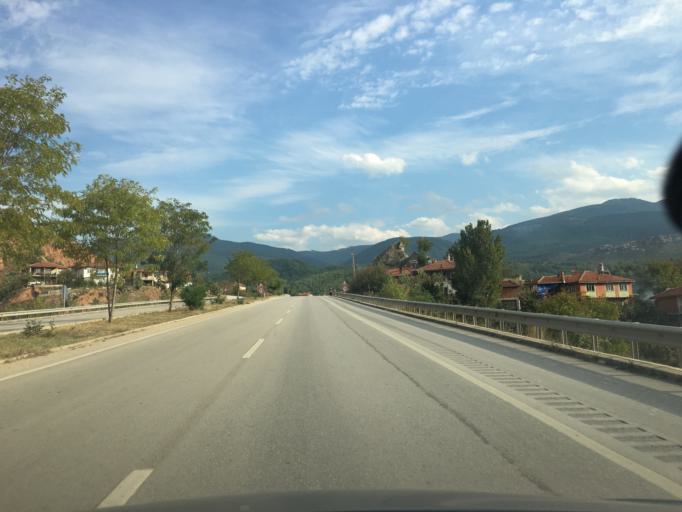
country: TR
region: Karabuk
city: Karabuk
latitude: 41.0977
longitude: 32.6742
